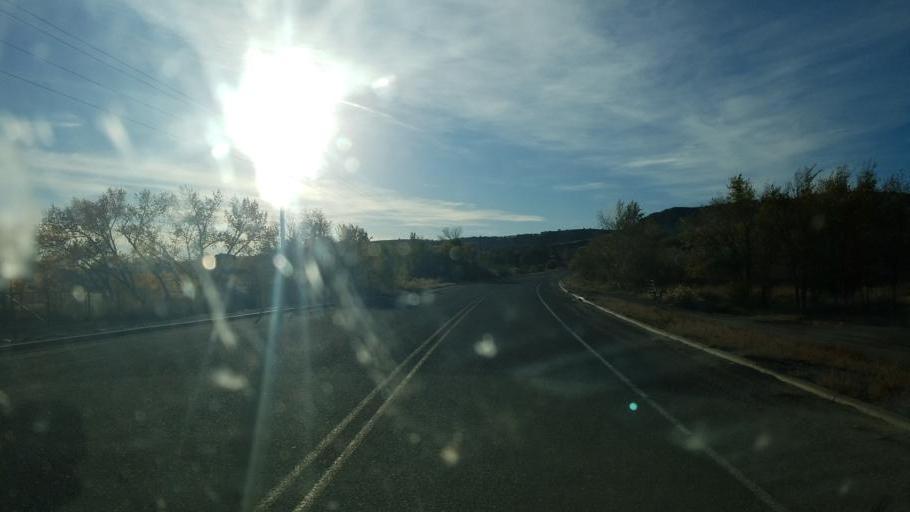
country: US
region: New Mexico
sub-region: San Juan County
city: Bloomfield
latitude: 36.7239
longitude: -107.8202
